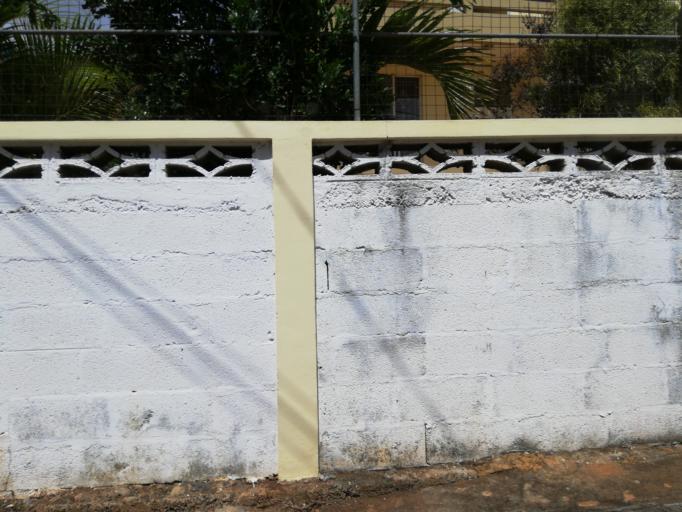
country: MU
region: Moka
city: Pailles
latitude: -20.2047
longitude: 57.4728
